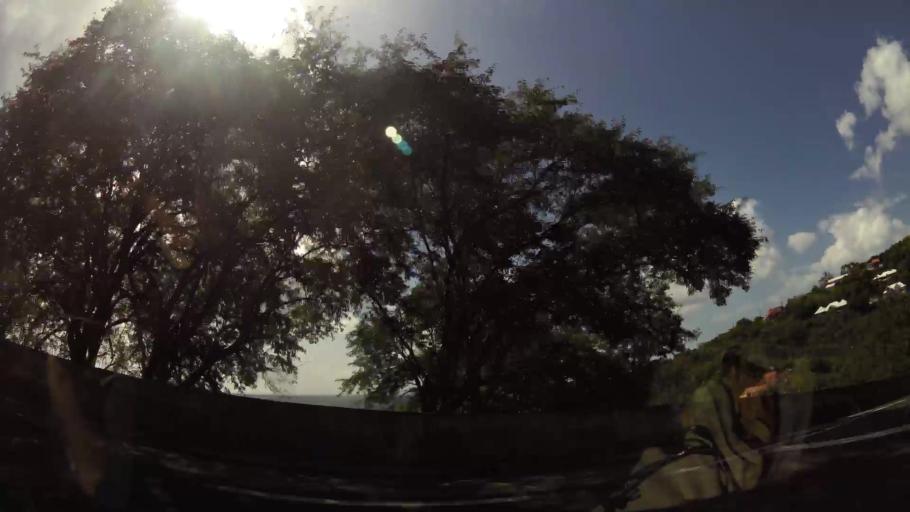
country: MQ
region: Martinique
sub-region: Martinique
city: Fort-de-France
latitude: 14.6294
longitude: -61.1189
